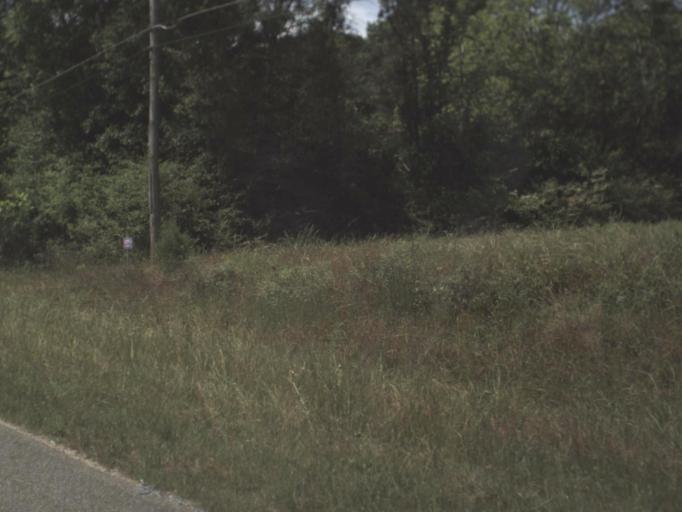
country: US
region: Florida
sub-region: Jackson County
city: Marianna
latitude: 30.7234
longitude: -85.2305
